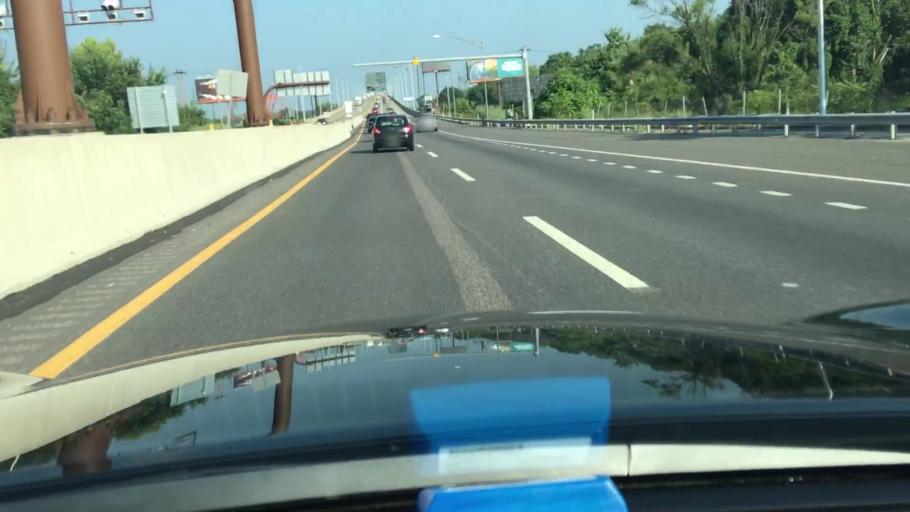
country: US
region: Pennsylvania
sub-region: Bucks County
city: Bristol
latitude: 40.1210
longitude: -74.8450
